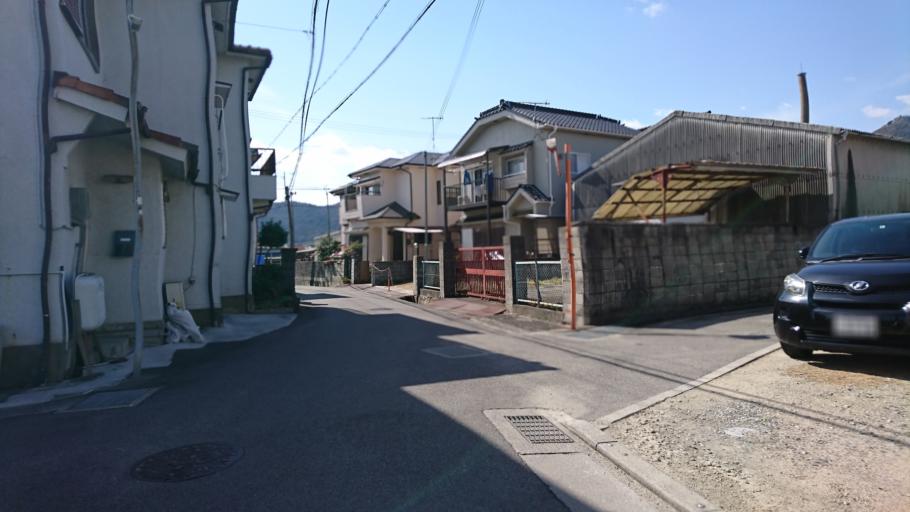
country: JP
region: Hyogo
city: Kakogawacho-honmachi
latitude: 34.8099
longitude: 134.8129
